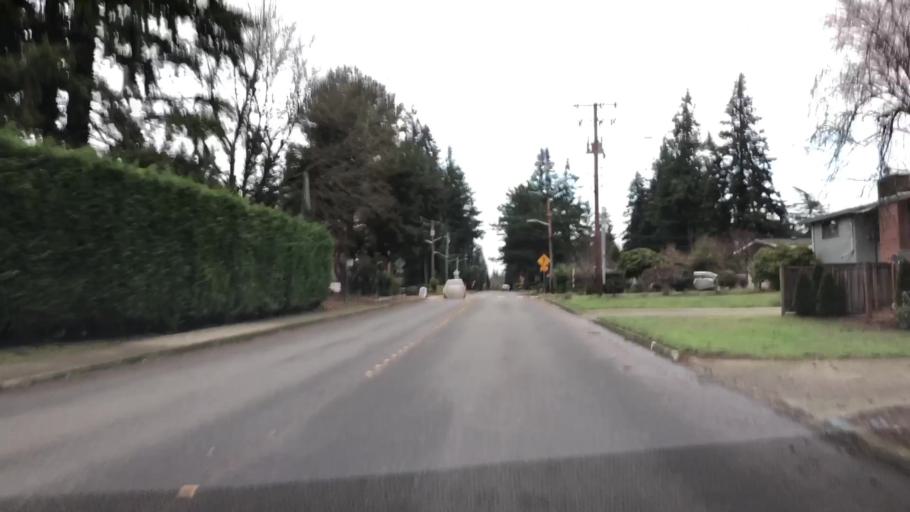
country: US
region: Washington
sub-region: King County
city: West Lake Sammamish
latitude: 47.6126
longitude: -122.1215
